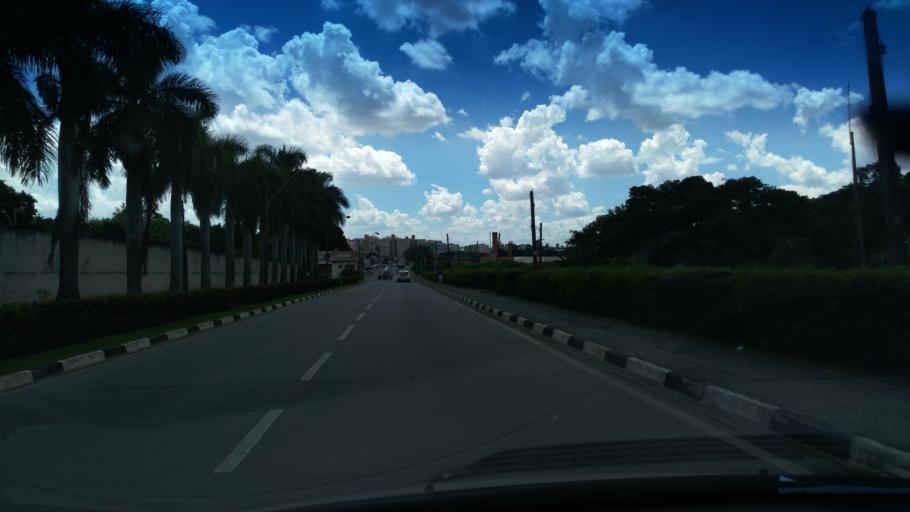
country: BR
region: Sao Paulo
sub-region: Vinhedo
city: Vinhedo
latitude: -23.0066
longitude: -46.9862
